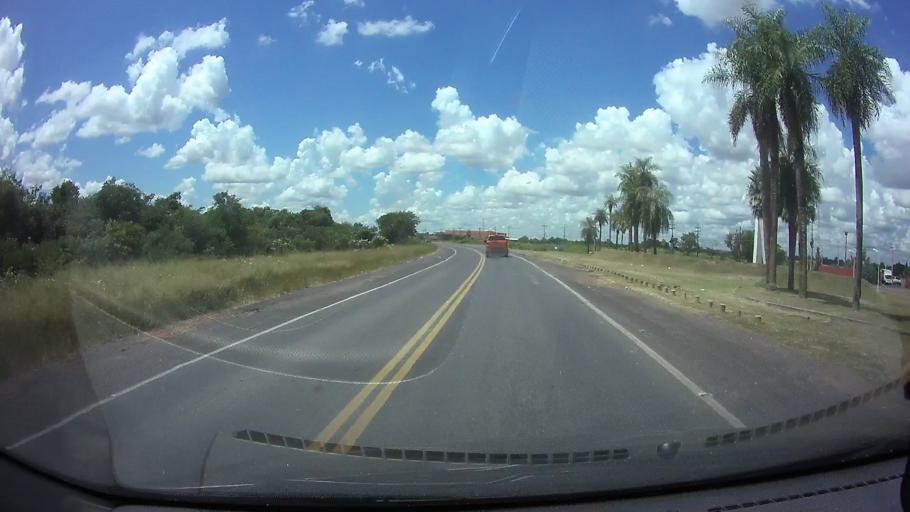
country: PY
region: Central
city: Colonia Mariano Roque Alonso
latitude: -25.1876
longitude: -57.5967
